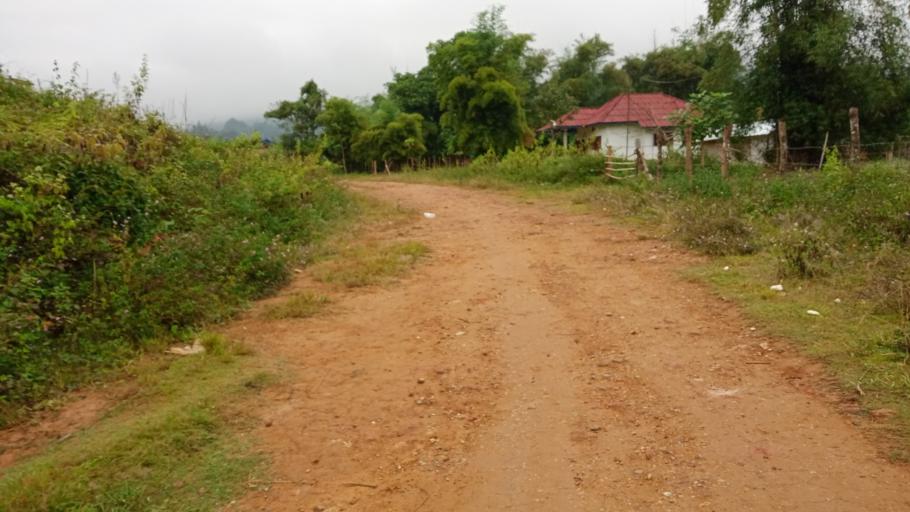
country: LA
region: Xiangkhoang
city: Phonsavan
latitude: 19.1019
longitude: 102.9293
